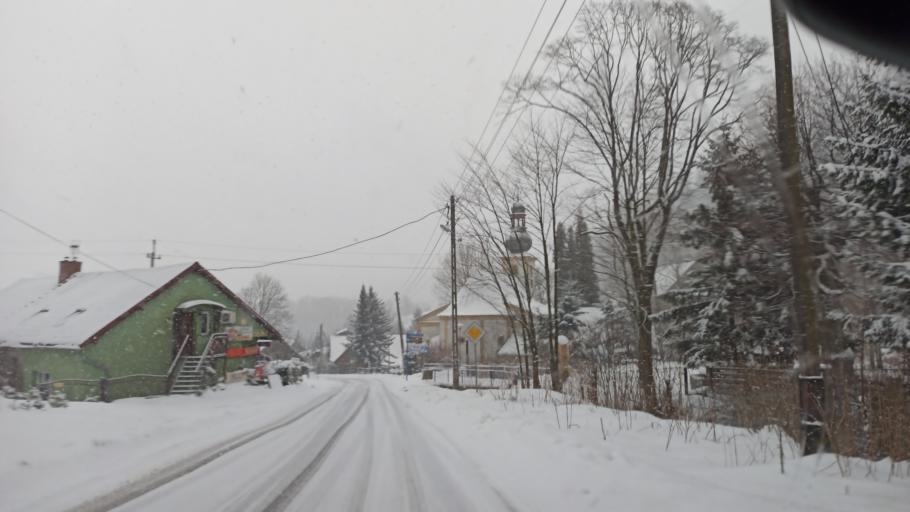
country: PL
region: Lower Silesian Voivodeship
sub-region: Powiat klodzki
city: Ludwikowice Klodzkie
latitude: 50.6558
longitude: 16.4737
